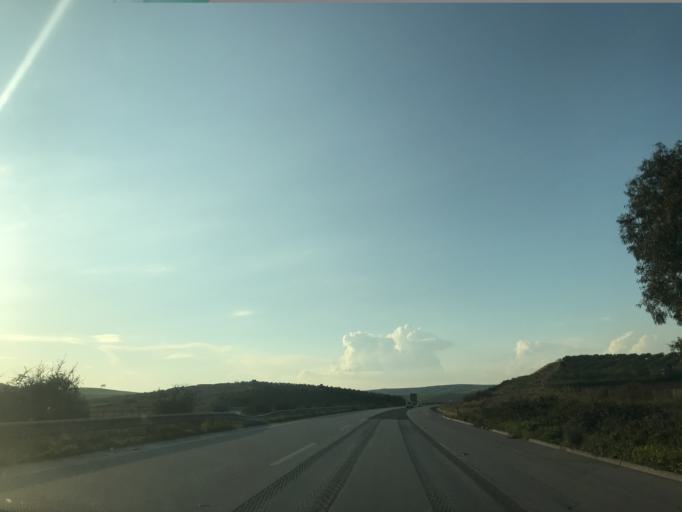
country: TR
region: Osmaniye
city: Toprakkale
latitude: 36.9765
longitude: 36.0065
